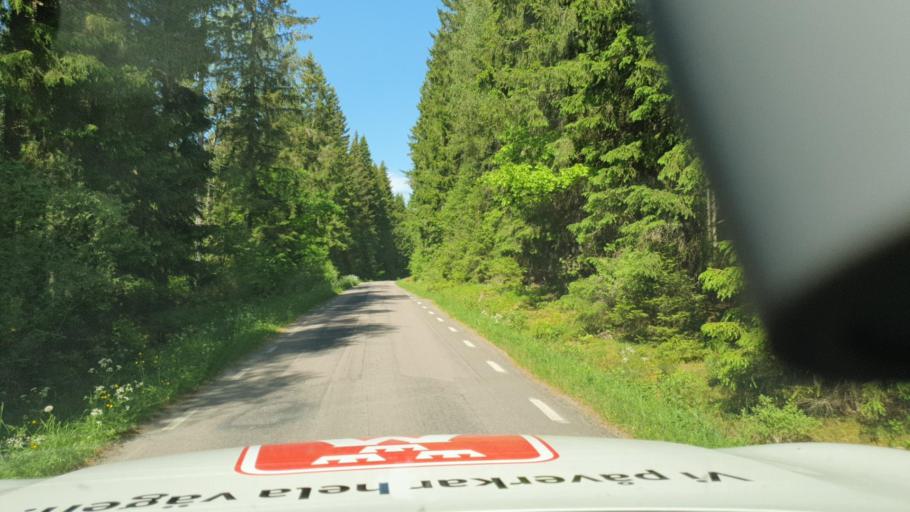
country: SE
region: Vaestra Goetaland
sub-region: Herrljunga Kommun
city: Herrljunga
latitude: 58.1394
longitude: 13.0772
